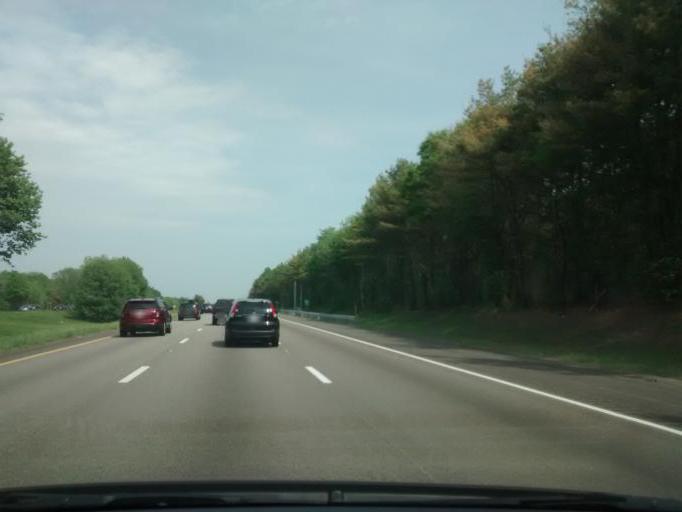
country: US
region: Massachusetts
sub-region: Bristol County
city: Norton Center
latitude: 41.9977
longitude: -71.1997
